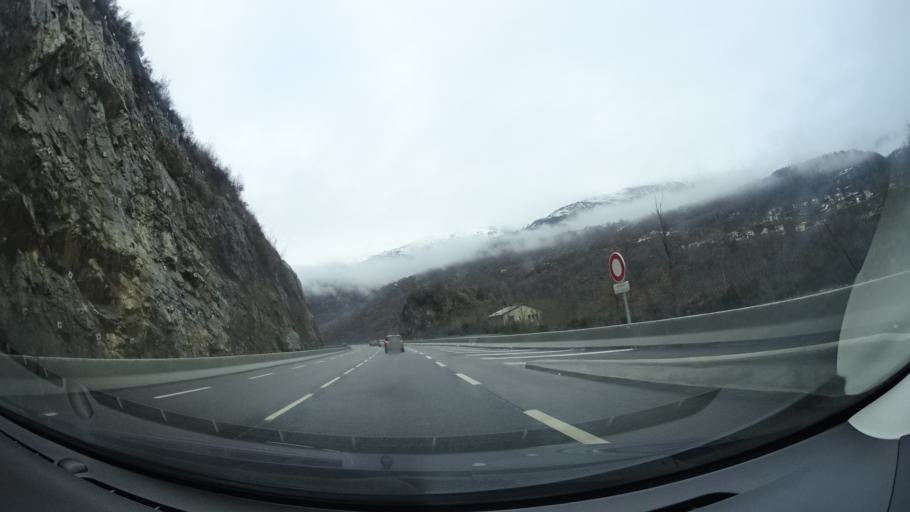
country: FR
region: Midi-Pyrenees
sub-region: Departement de l'Ariege
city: Ax-les-Thermes
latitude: 42.7204
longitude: 1.8332
